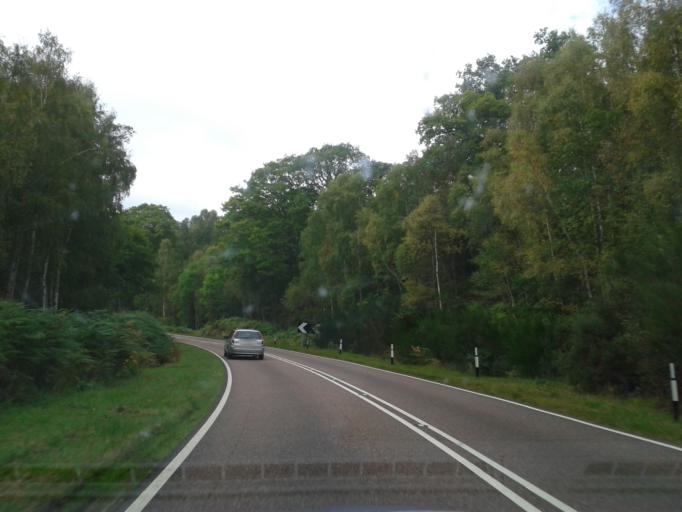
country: GB
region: Scotland
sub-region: Highland
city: Spean Bridge
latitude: 57.0811
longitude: -4.8490
